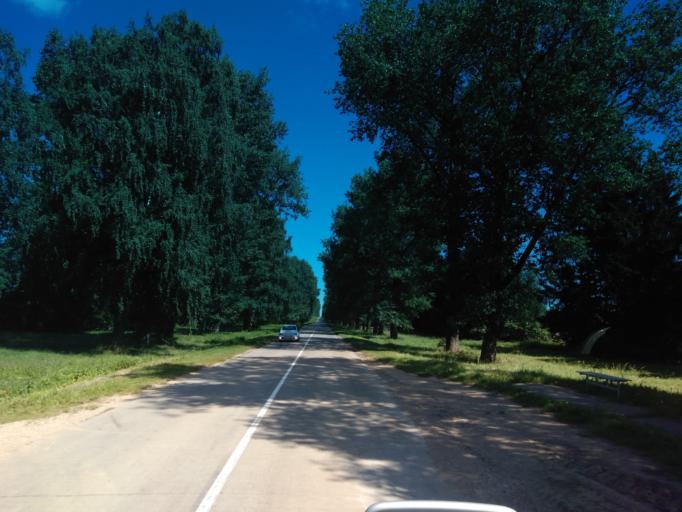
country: BY
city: Fanipol
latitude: 53.6691
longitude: 27.3411
